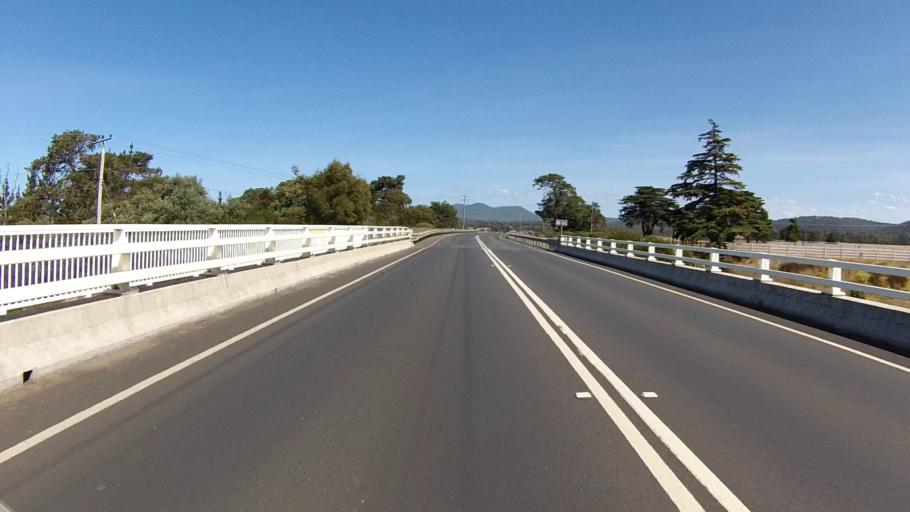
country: AU
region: Tasmania
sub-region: Sorell
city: Sorell
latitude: -42.5098
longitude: 147.9079
